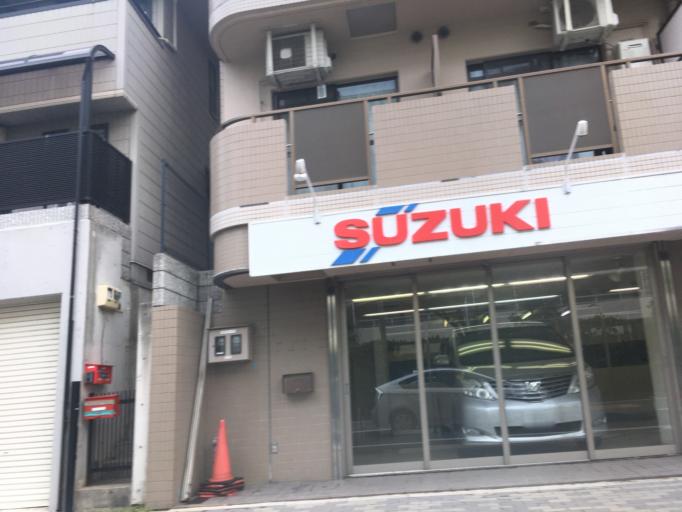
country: JP
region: Hyogo
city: Ashiya
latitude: 34.7193
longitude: 135.2445
